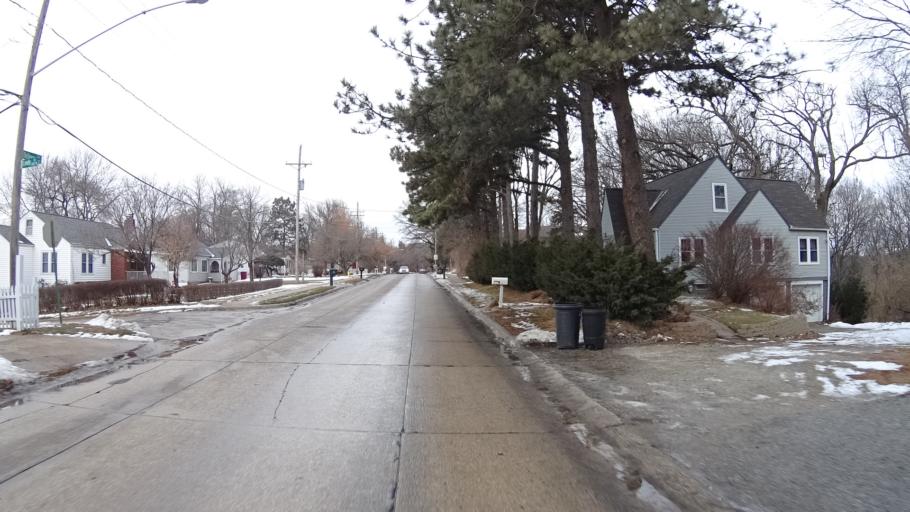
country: US
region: Nebraska
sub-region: Sarpy County
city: Bellevue
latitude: 41.1700
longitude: -95.9181
